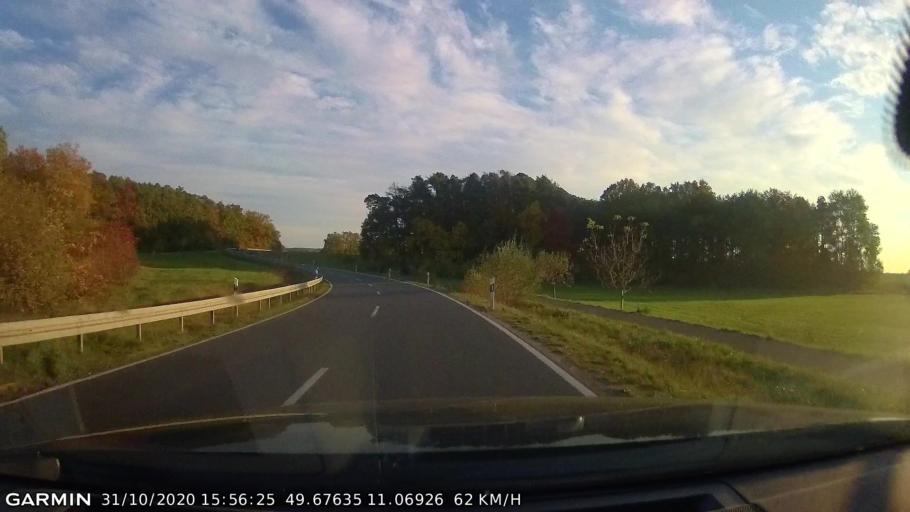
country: DE
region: Bavaria
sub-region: Upper Franconia
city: Poxdorf
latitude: 49.6762
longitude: 11.0695
